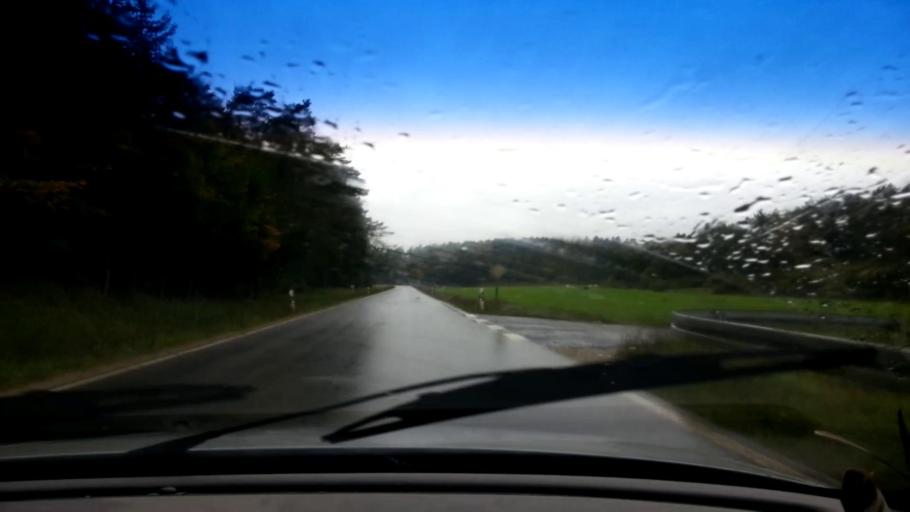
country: DE
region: Bavaria
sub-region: Upper Franconia
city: Konigsfeld
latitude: 49.9431
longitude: 11.1445
